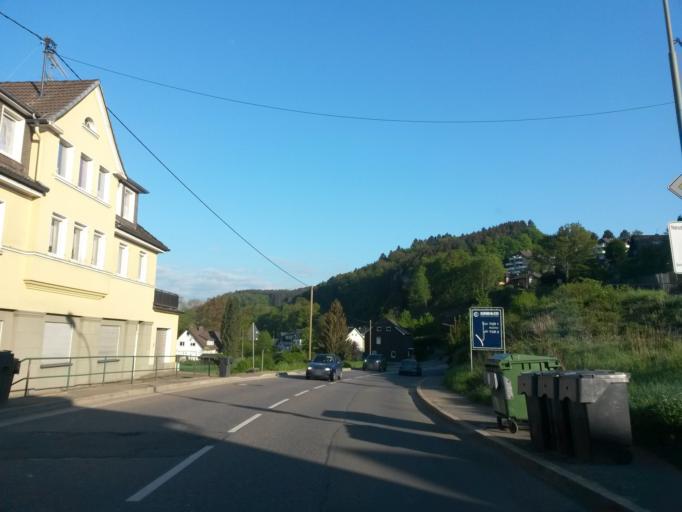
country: DE
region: North Rhine-Westphalia
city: Wiehl
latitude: 50.9621
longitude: 7.5096
